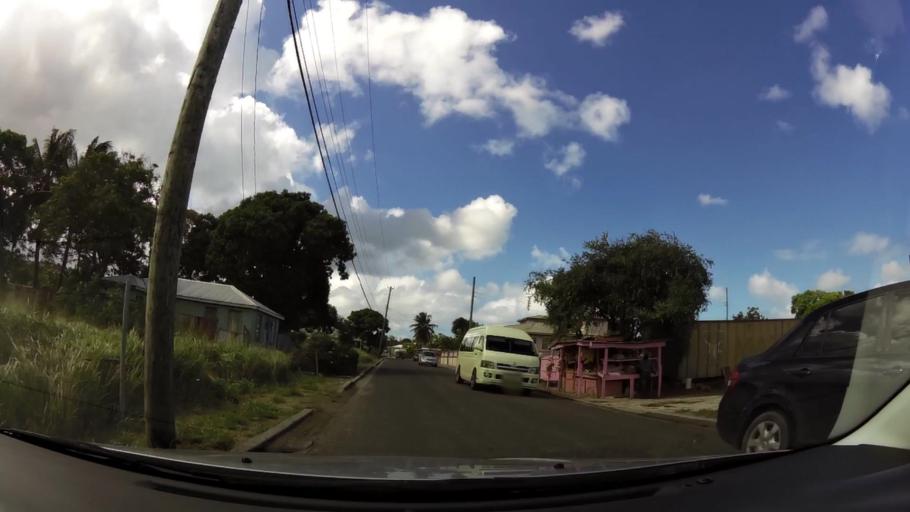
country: AG
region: Saint John
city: Saint John's
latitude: 17.1064
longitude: -61.8401
